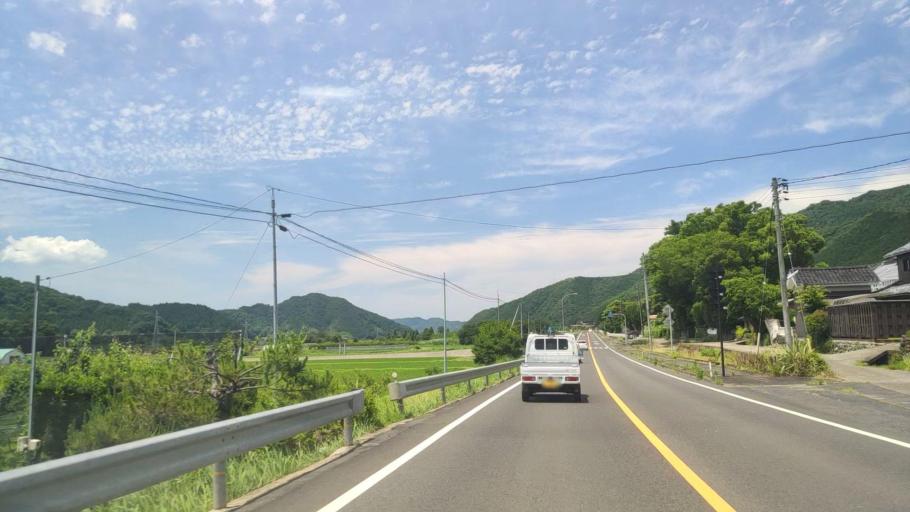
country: JP
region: Tottori
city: Tottori
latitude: 35.3679
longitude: 134.3127
